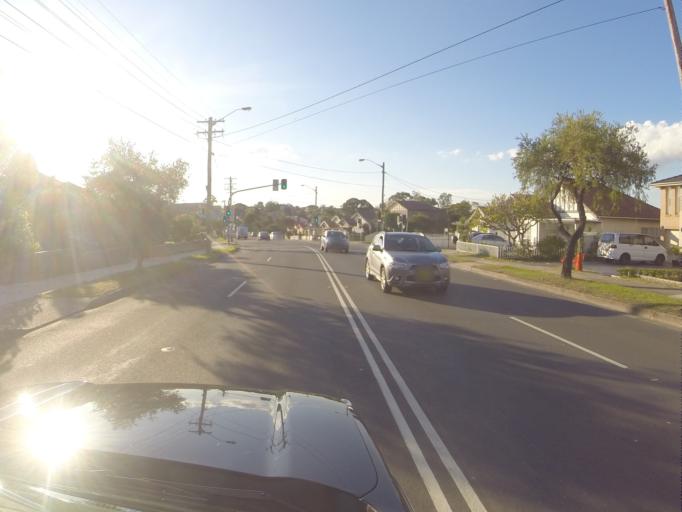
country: AU
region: New South Wales
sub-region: Rockdale
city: Bexley North
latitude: -33.9248
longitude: 151.1082
